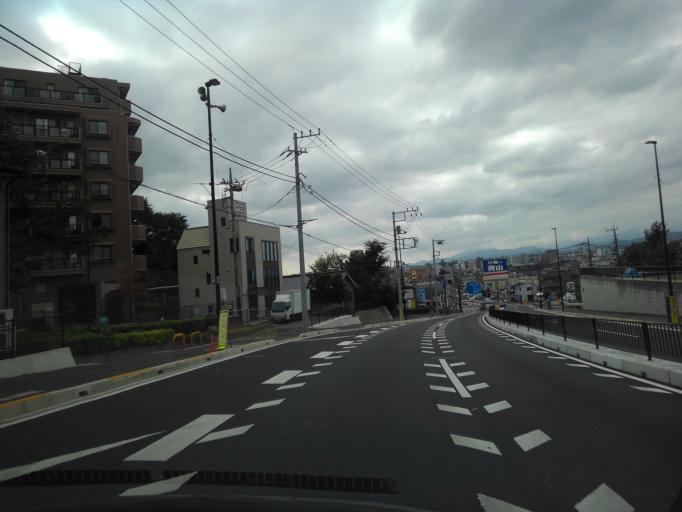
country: JP
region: Tokyo
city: Hachioji
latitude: 35.6737
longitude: 139.3325
